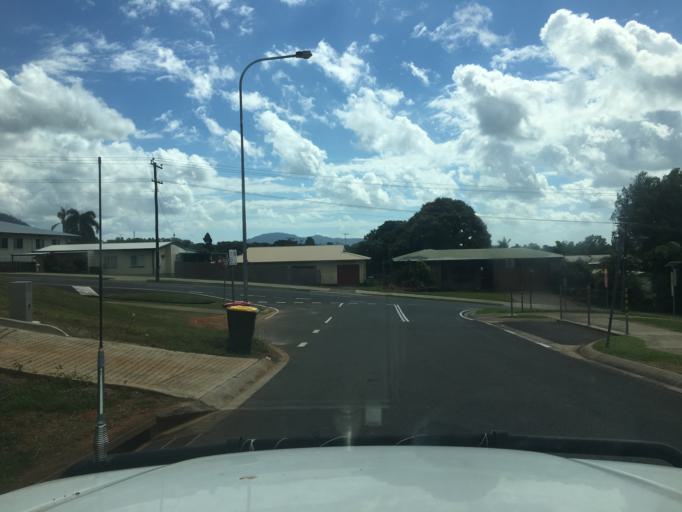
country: AU
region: Queensland
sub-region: Cairns
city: Woree
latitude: -16.9676
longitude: 145.7395
